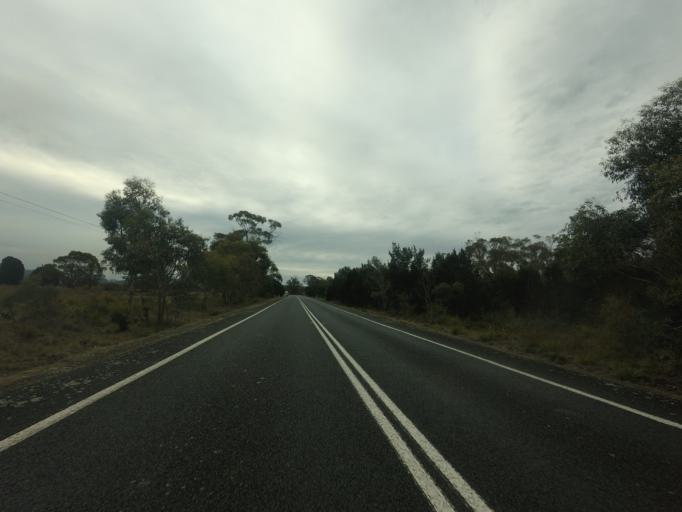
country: AU
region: Tasmania
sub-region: Break O'Day
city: St Helens
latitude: -42.0552
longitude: 148.0578
